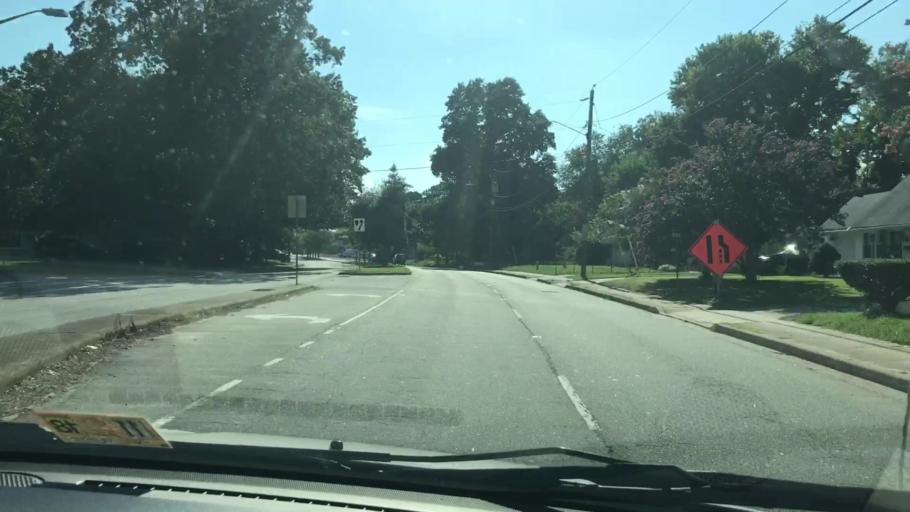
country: US
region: Virginia
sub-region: City of Norfolk
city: Norfolk
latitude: 36.8966
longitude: -76.2196
